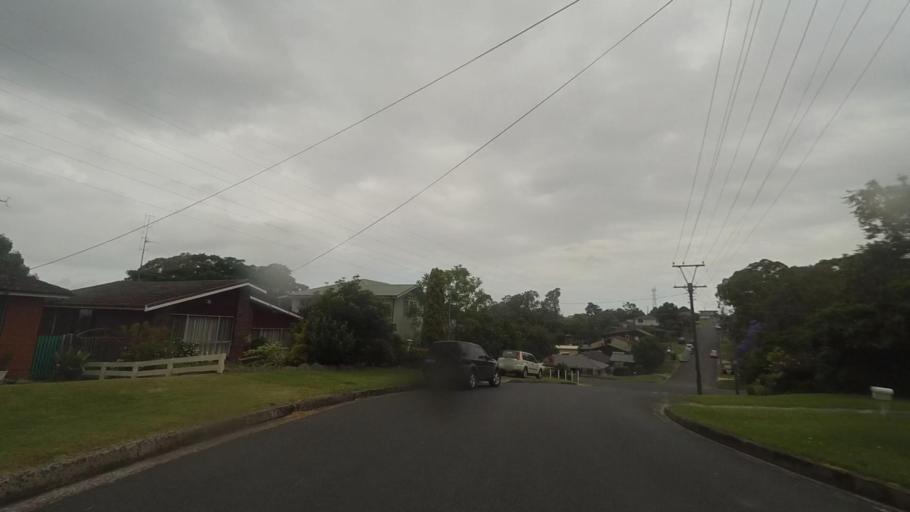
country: AU
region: New South Wales
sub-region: Wollongong
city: Cordeaux Heights
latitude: -34.4545
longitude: 150.8179
